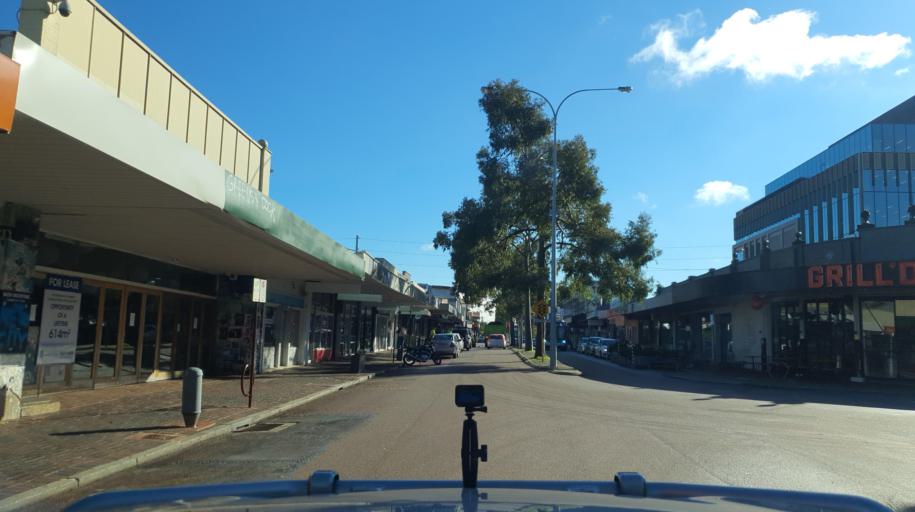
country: AU
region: Western Australia
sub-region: Vincent
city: Leederville
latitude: -31.9376
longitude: 115.8412
